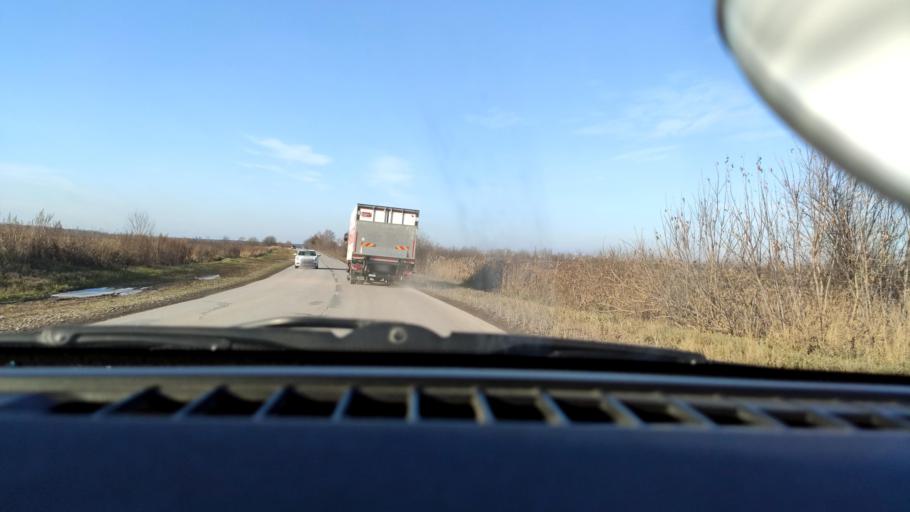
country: RU
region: Perm
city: Kondratovo
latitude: 57.9964
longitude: 56.0853
